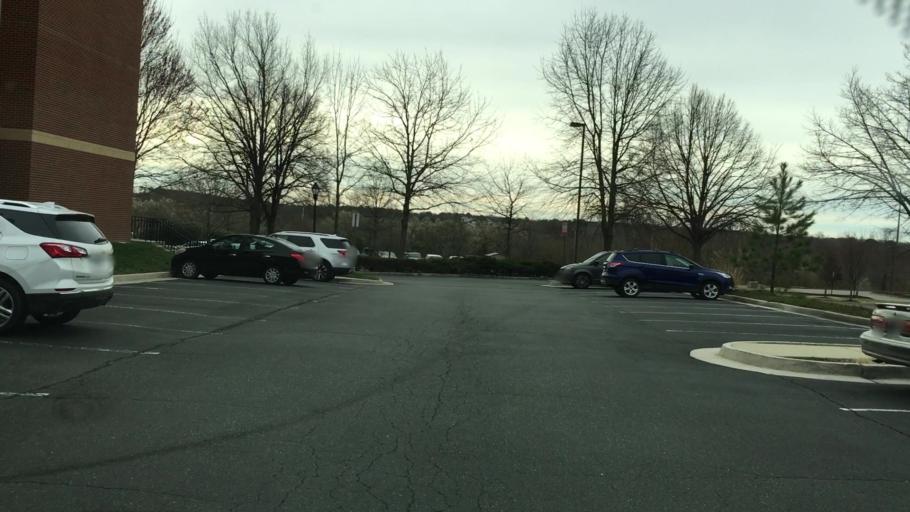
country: US
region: Virginia
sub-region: Henrico County
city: Short Pump
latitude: 37.6442
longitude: -77.5777
